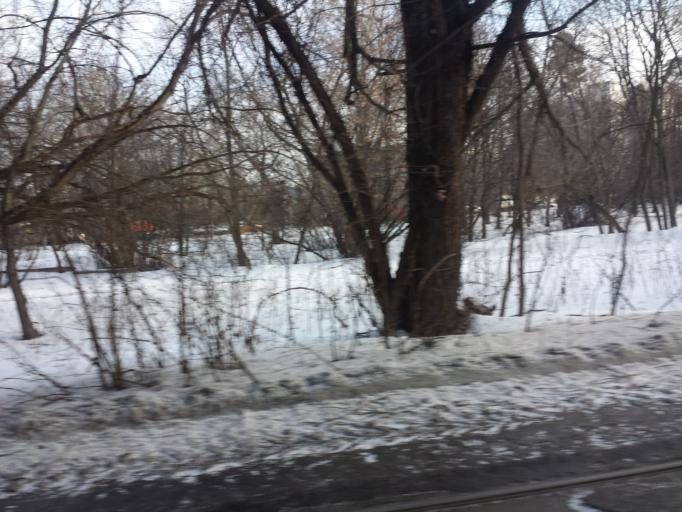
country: RU
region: Moscow
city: Pokrovskoye-Streshnevo
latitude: 55.8123
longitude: 37.4743
